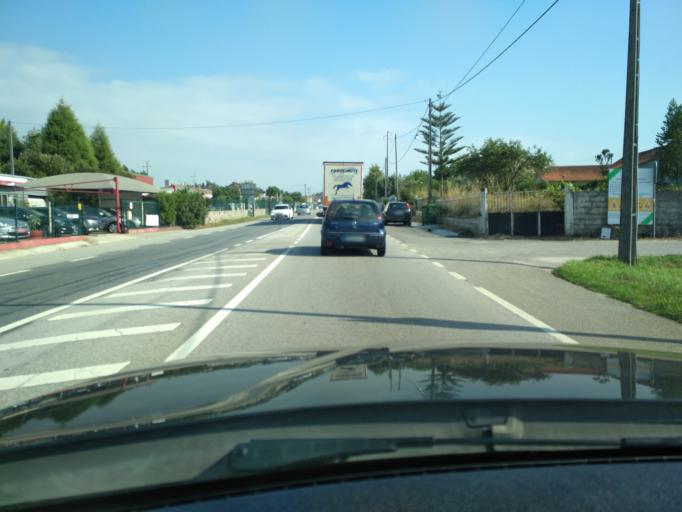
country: PT
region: Aveiro
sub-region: Mealhada
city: Pampilhosa do Botao
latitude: 40.3117
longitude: -8.4502
